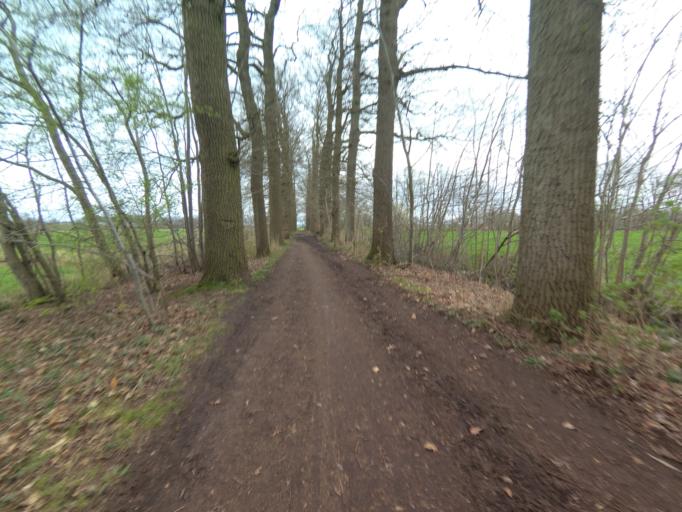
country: NL
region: Gelderland
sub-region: Gemeente Barneveld
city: Zwartebroek
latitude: 52.1534
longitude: 5.4749
